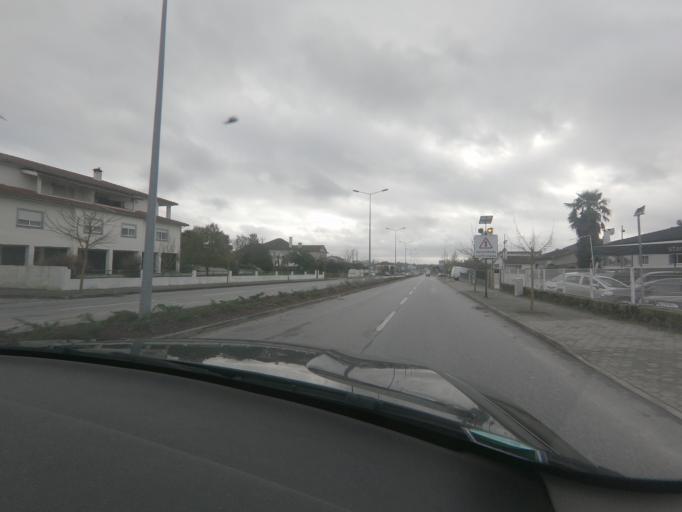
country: PT
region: Viseu
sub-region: Viseu
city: Abraveses
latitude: 40.6898
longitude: -7.9272
